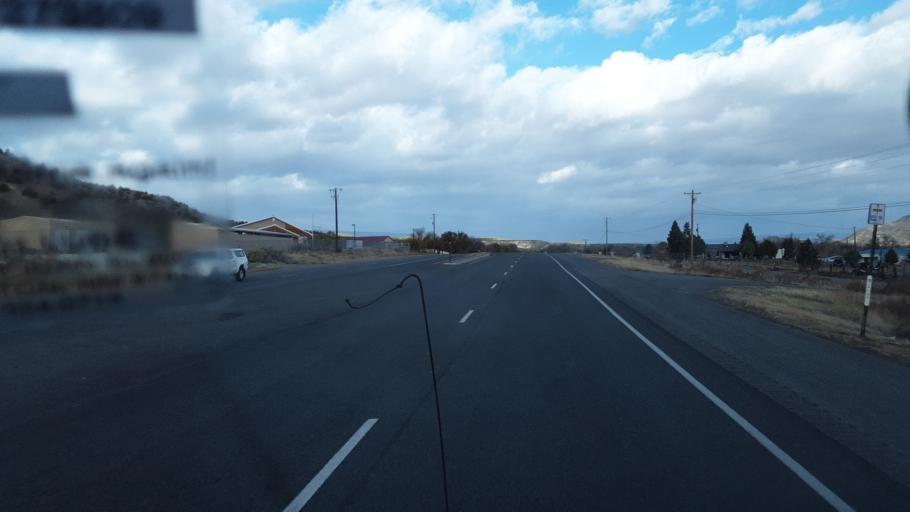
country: US
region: New Mexico
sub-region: Rio Arriba County
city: Ohkay Owingeh
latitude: 36.0379
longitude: -106.0973
